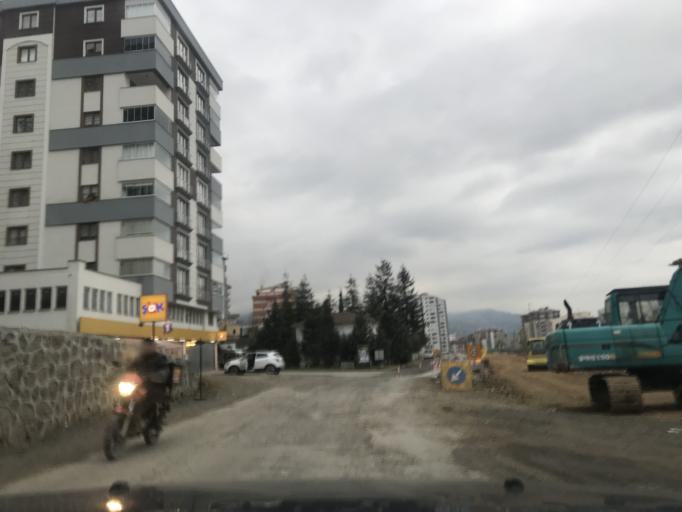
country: TR
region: Trabzon
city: Akcaabat
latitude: 41.0071
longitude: 39.6095
